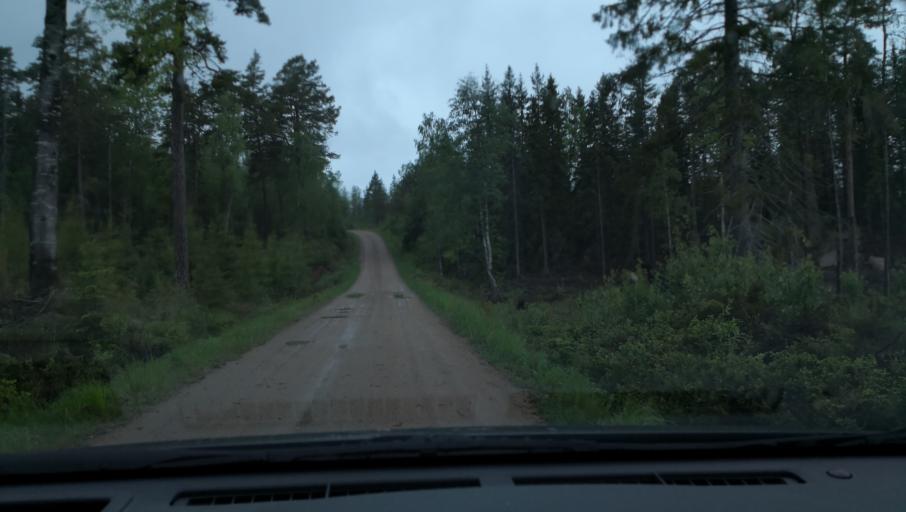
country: SE
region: Uppsala
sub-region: Enkopings Kommun
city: Orsundsbro
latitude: 59.9317
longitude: 17.3284
